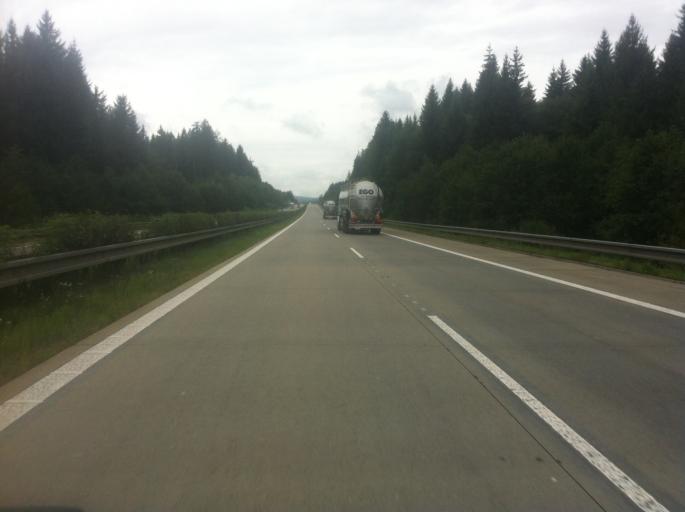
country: CZ
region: Plzensky
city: Primda
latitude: 49.7047
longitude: 12.6978
